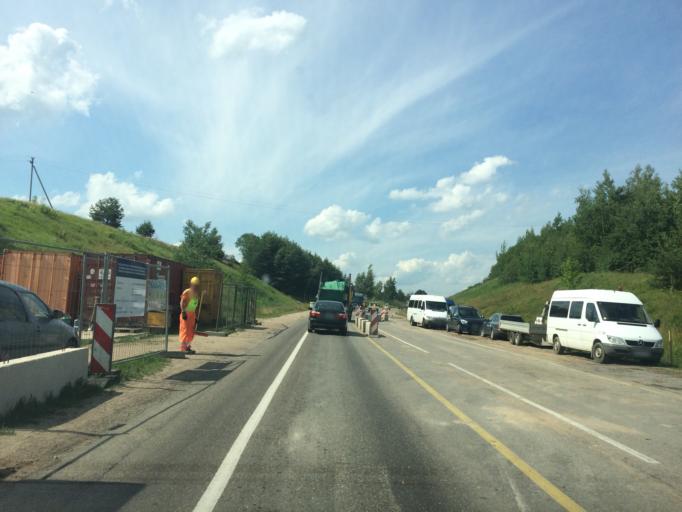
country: LT
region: Kauno apskritis
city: Jonava
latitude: 55.0890
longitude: 24.3140
